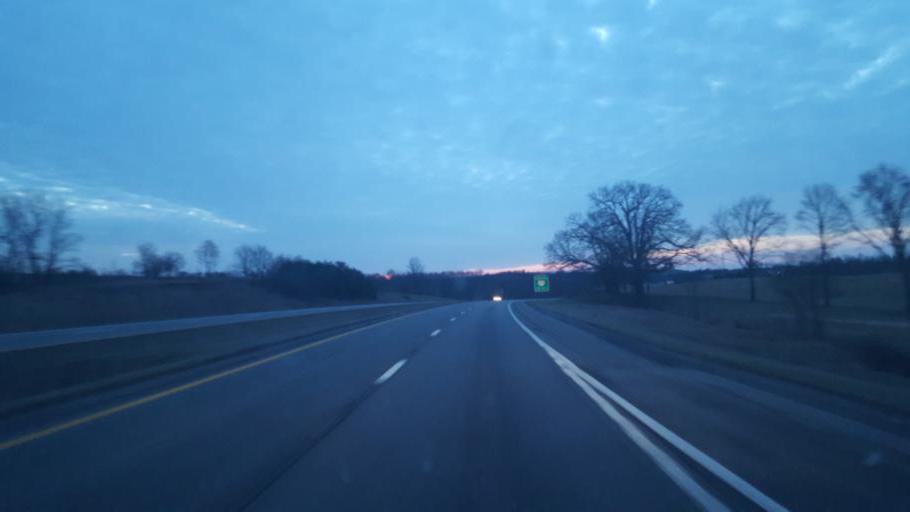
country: US
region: Ohio
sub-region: Jackson County
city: Jackson
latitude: 38.9972
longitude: -82.5486
